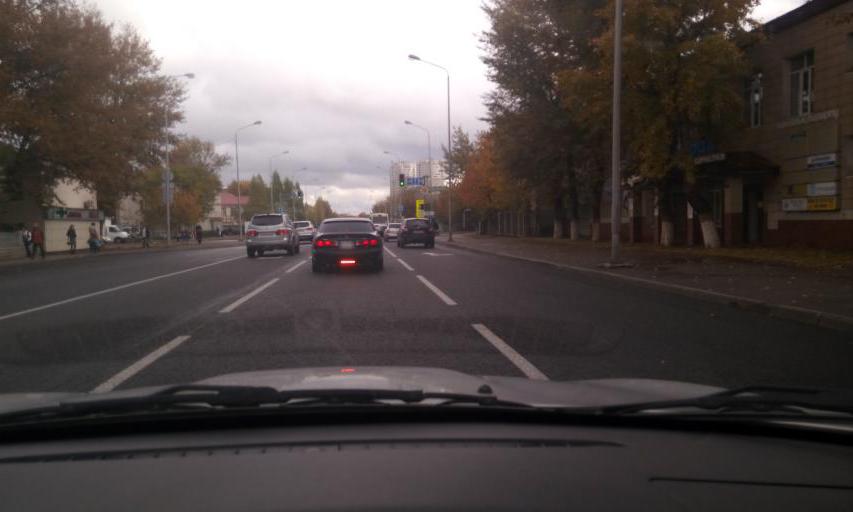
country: KZ
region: Astana Qalasy
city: Astana
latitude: 51.1684
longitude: 71.4559
